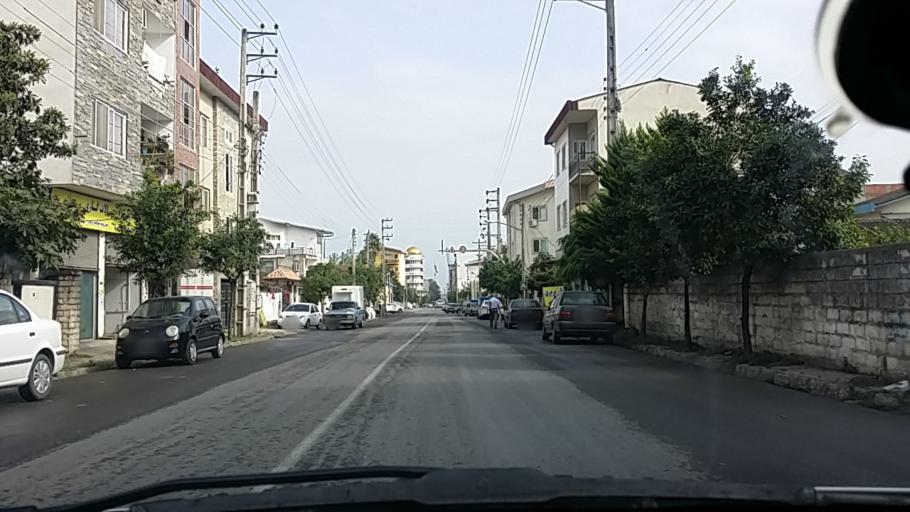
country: IR
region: Mazandaran
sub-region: Nowshahr
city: Nowshahr
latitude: 36.6457
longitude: 51.5084
